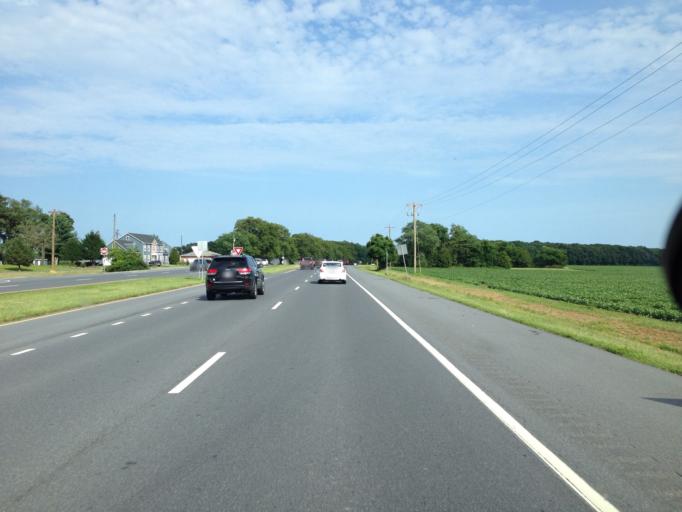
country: US
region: Delaware
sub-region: Sussex County
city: Milton
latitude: 38.7888
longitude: -75.2484
